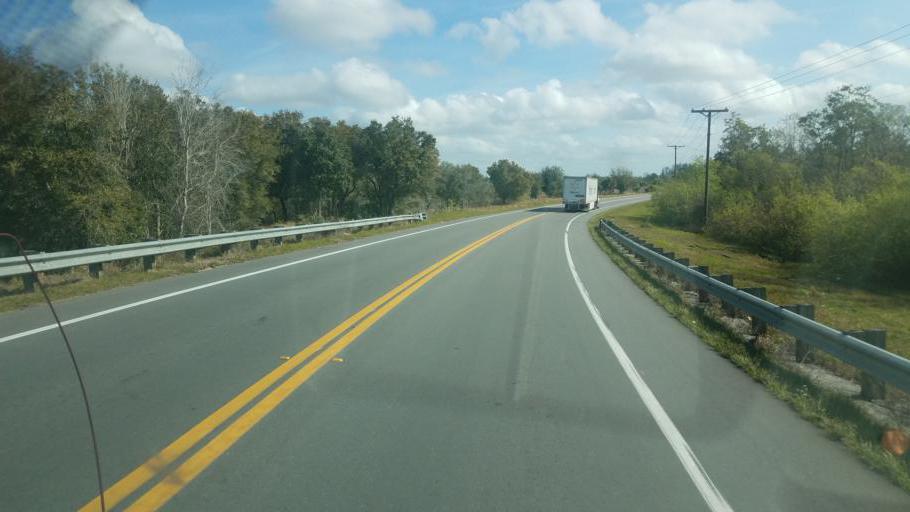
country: US
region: Florida
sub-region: Polk County
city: Lake Alfred
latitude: 28.1679
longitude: -81.7182
